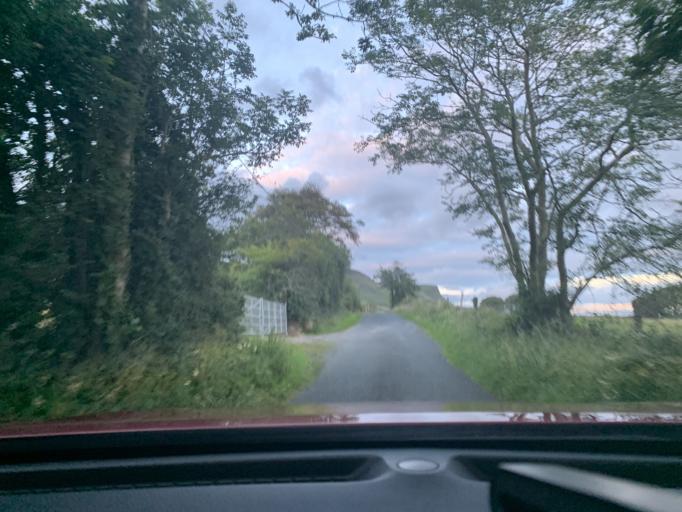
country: IE
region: Connaught
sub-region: Sligo
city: Sligo
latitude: 54.3566
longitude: -8.4999
